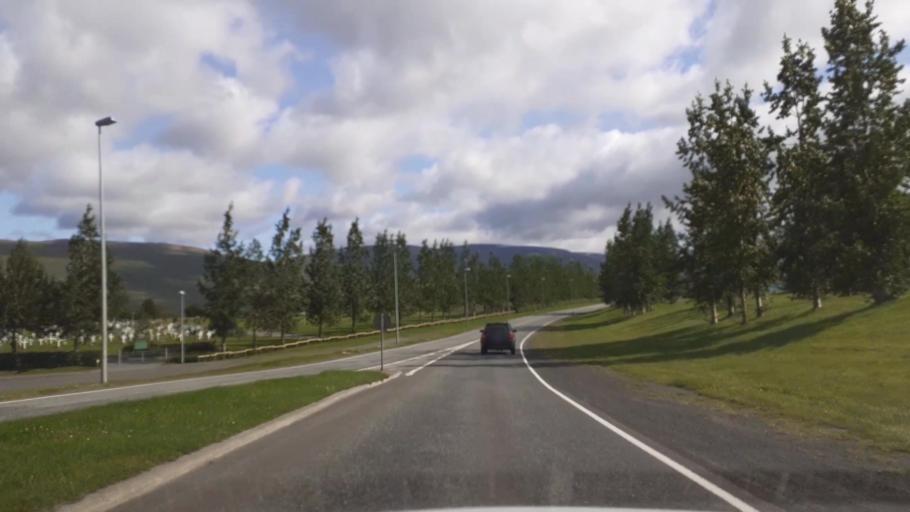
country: IS
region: Northeast
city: Akureyri
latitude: 65.6677
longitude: -18.0960
